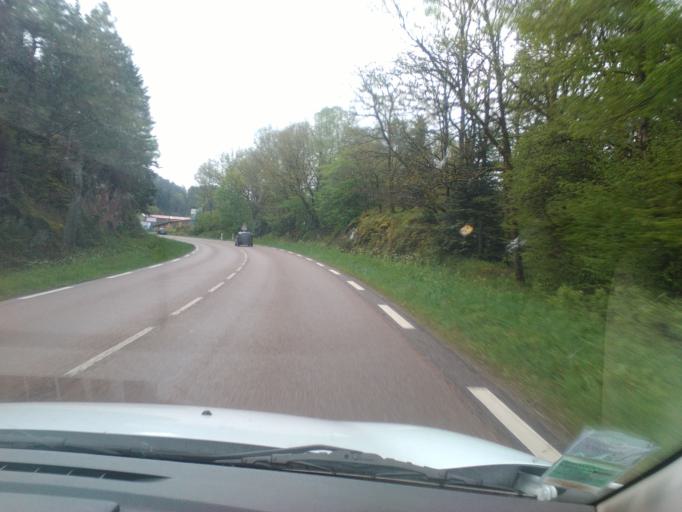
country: FR
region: Lorraine
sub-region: Departement des Vosges
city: Vagney
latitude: 47.9825
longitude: 6.7231
